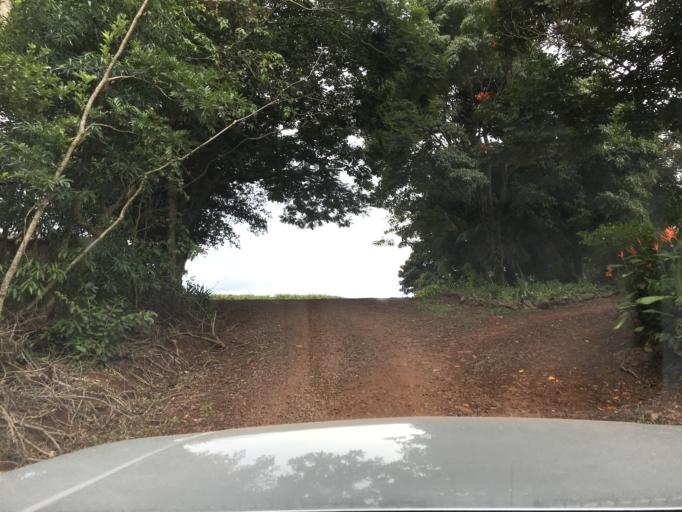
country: BR
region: Parana
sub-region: Palotina
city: Palotina
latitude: -24.2723
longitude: -53.7862
